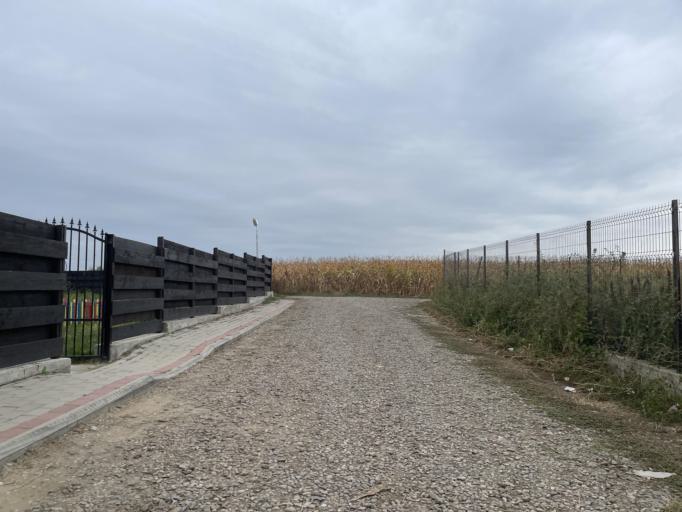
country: RO
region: Iasi
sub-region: Comuna Dumesti
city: Dumesti
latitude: 47.1716
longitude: 27.3381
